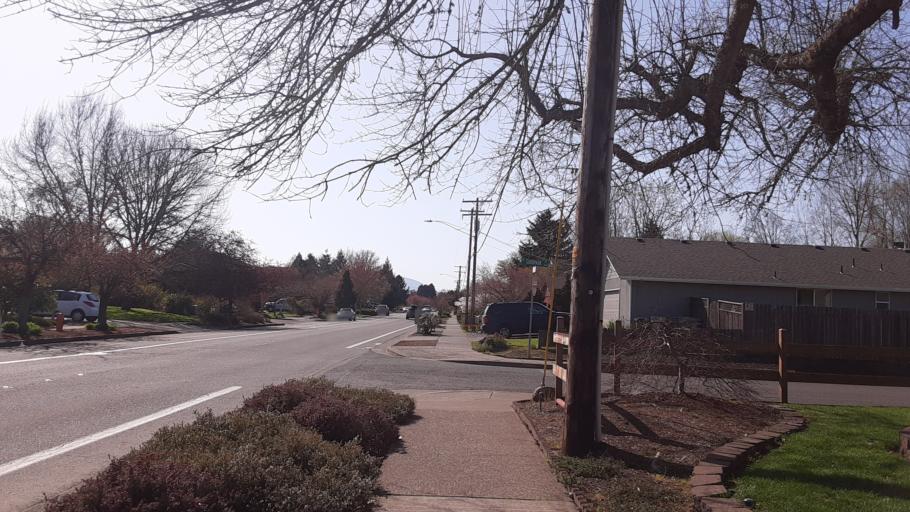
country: US
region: Oregon
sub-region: Benton County
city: Corvallis
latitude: 44.5369
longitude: -123.2580
